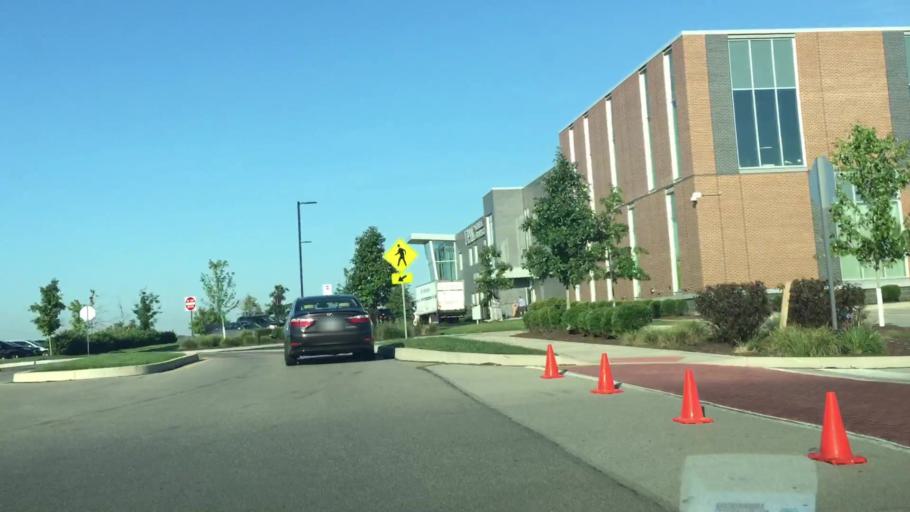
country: US
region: Pennsylvania
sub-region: Butler County
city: Cranberry Township
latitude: 40.6872
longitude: -80.0931
